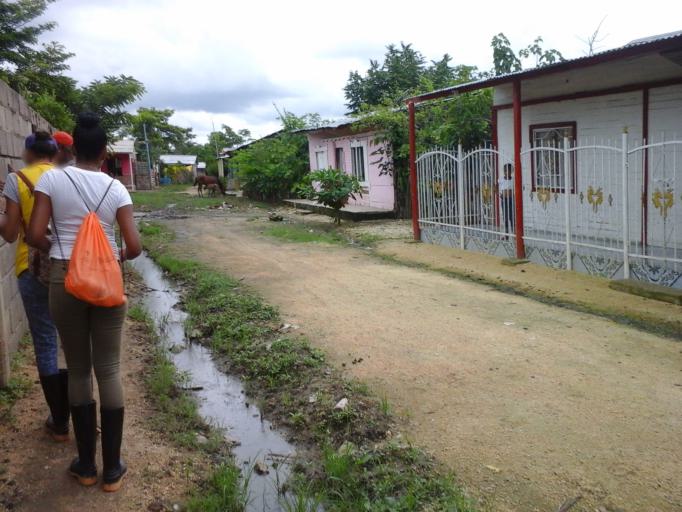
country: CO
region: Bolivar
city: San Pablo
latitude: 10.1444
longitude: -75.2755
